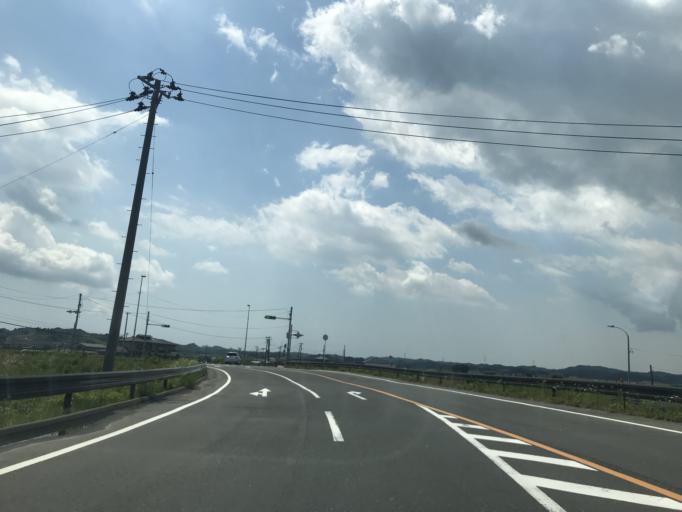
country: JP
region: Miyagi
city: Matsushima
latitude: 38.4554
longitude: 141.0863
